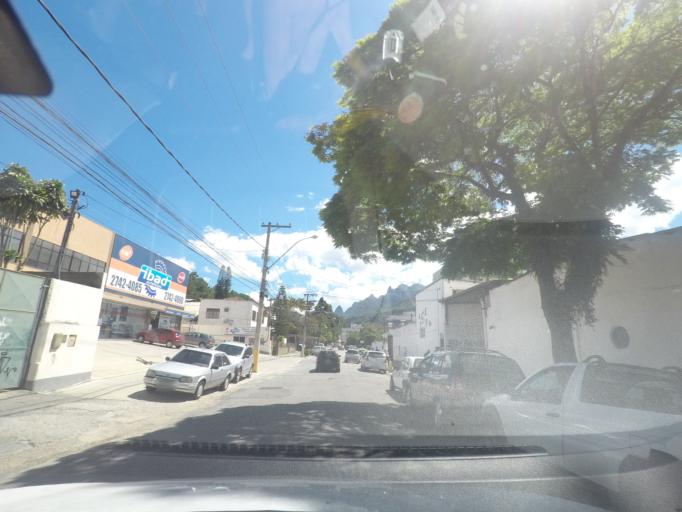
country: BR
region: Rio de Janeiro
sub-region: Teresopolis
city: Teresopolis
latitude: -22.4192
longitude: -42.9728
